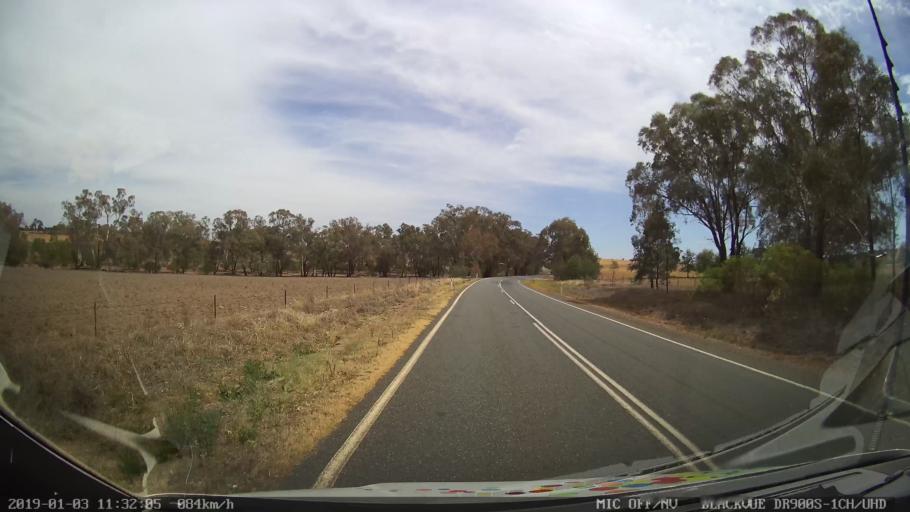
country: AU
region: New South Wales
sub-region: Weddin
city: Grenfell
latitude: -33.9627
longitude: 148.1804
